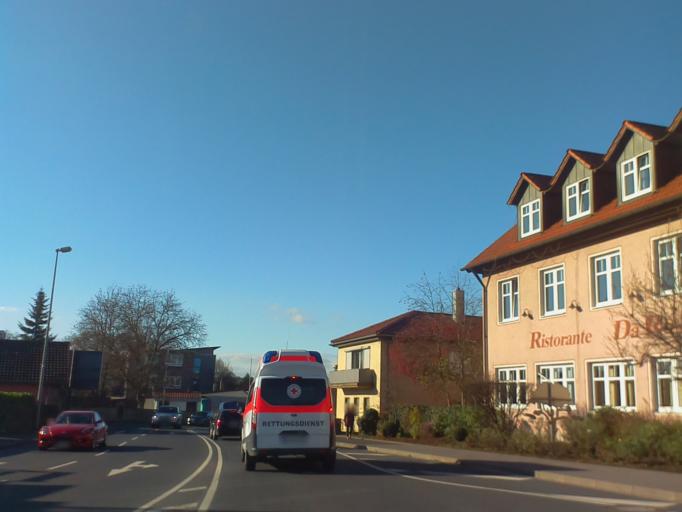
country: DE
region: Bavaria
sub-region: Regierungsbezirk Unterfranken
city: Bad Neustadt an der Saale
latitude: 50.3209
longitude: 10.2120
